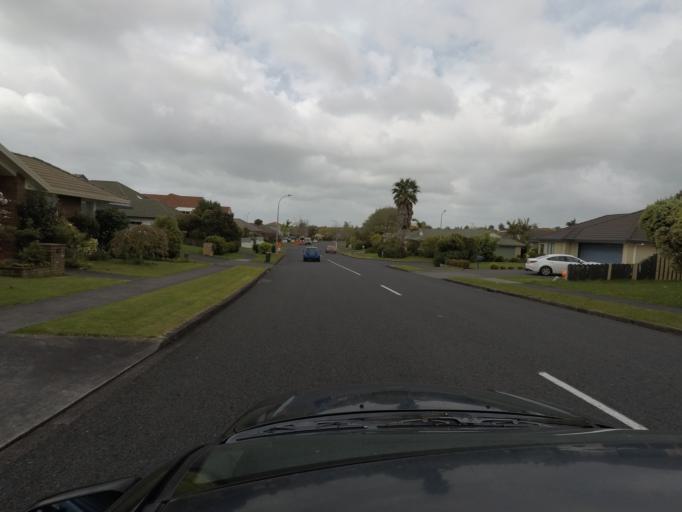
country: NZ
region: Auckland
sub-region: Auckland
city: Pakuranga
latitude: -36.9255
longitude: 174.9172
